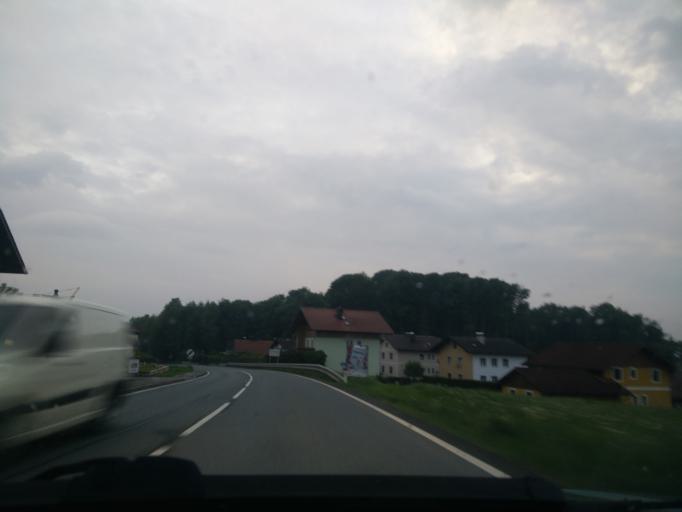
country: AT
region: Salzburg
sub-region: Politischer Bezirk Salzburg-Umgebung
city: Elixhausen
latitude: 47.8836
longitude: 13.0655
